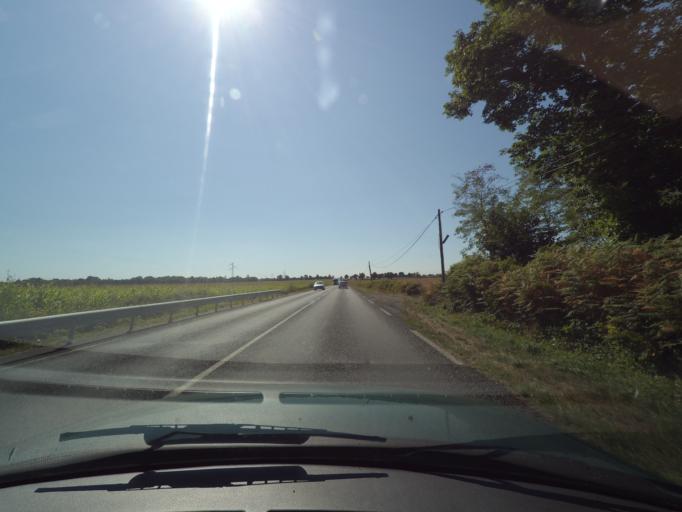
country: FR
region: Limousin
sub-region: Departement de la Haute-Vienne
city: Bellac
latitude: 46.0831
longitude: 1.0882
